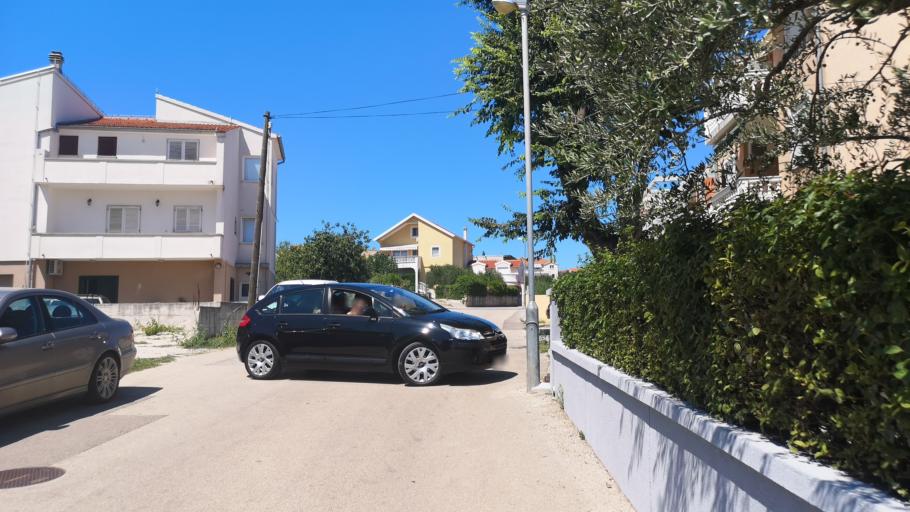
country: HR
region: Sibensko-Kniniska
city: Vodice
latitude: 43.7609
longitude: 15.7694
